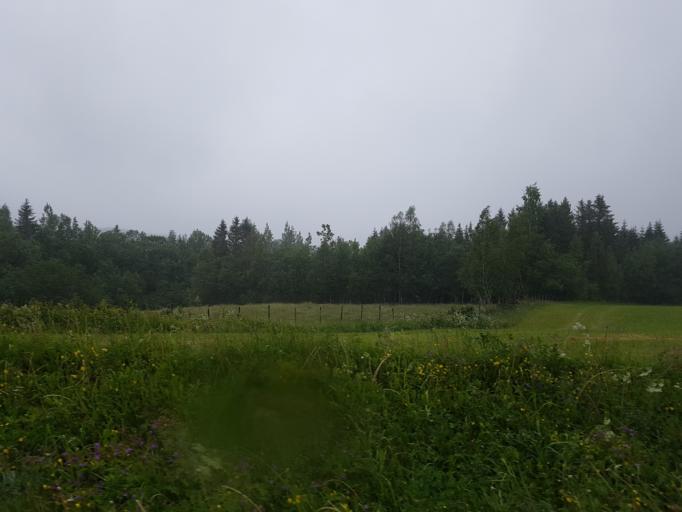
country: NO
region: Sor-Trondelag
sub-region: Selbu
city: Mebonden
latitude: 63.3779
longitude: 11.0803
